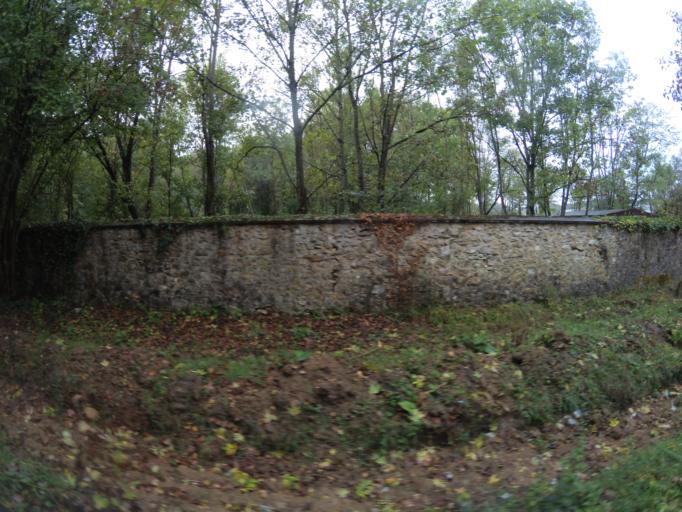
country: FR
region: Ile-de-France
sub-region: Departement de Seine-et-Marne
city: Croissy-Beaubourg
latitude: 48.8247
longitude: 2.6653
